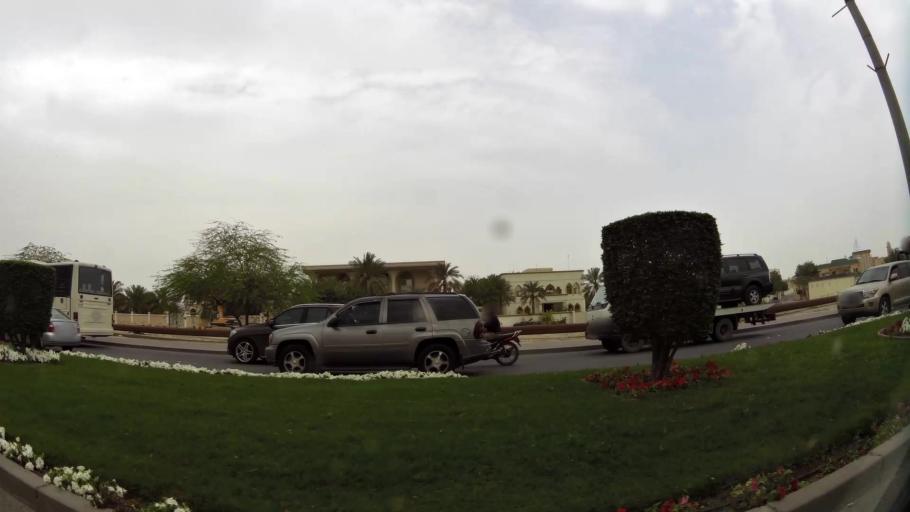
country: BH
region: Northern
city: Ar Rifa'
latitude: 26.1326
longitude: 50.5418
